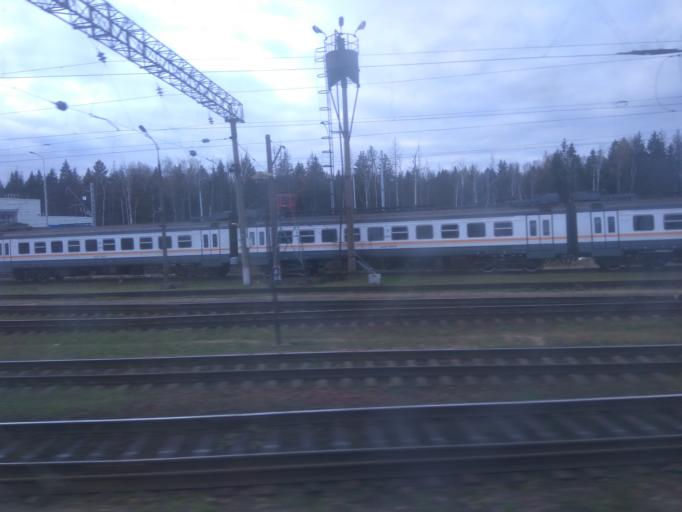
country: RU
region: Moskovskaya
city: Aprelevka
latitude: 55.5621
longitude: 37.0902
